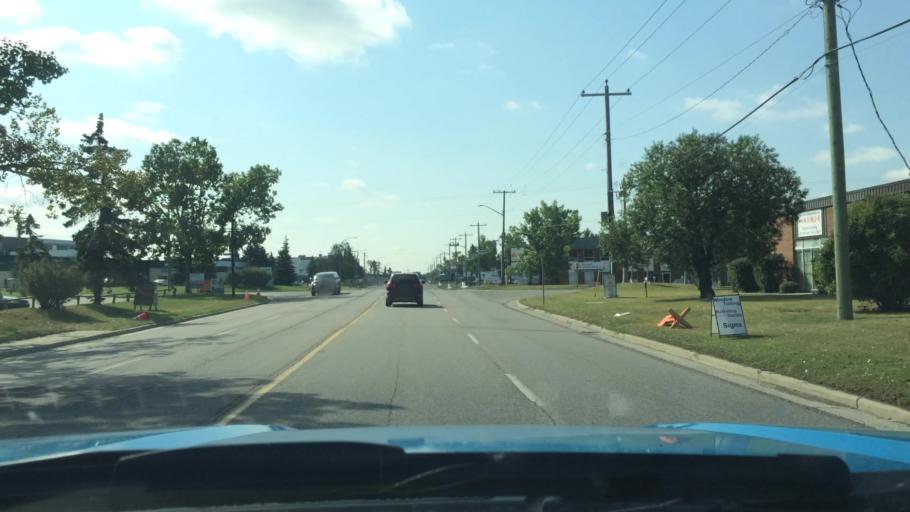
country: CA
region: Alberta
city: Calgary
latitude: 51.0895
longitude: -114.0322
